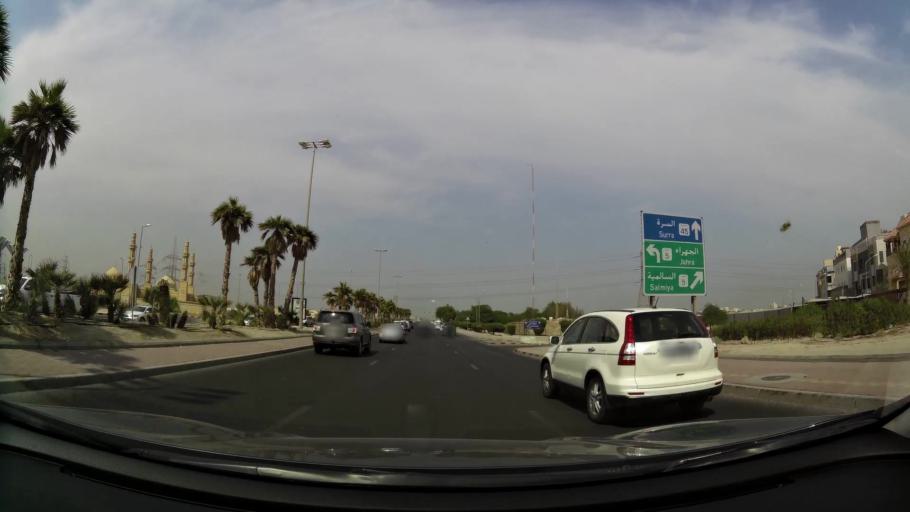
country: KW
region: Al Farwaniyah
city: Janub as Surrah
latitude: 29.3022
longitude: 48.0011
